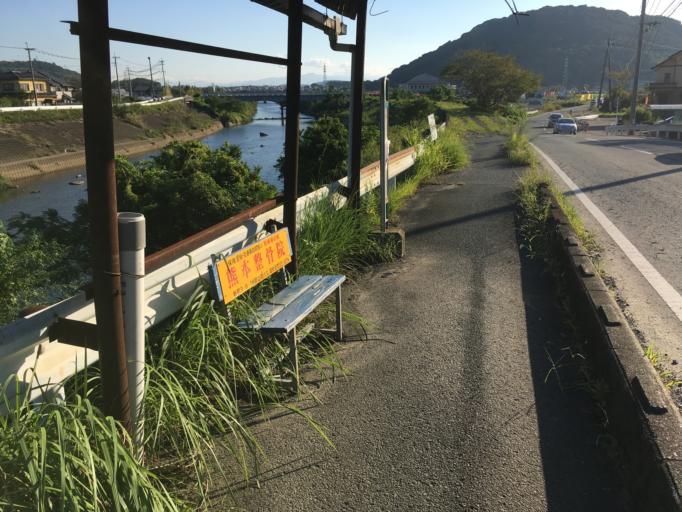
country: JP
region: Kumamoto
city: Kumamoto
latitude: 32.7912
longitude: 130.6682
